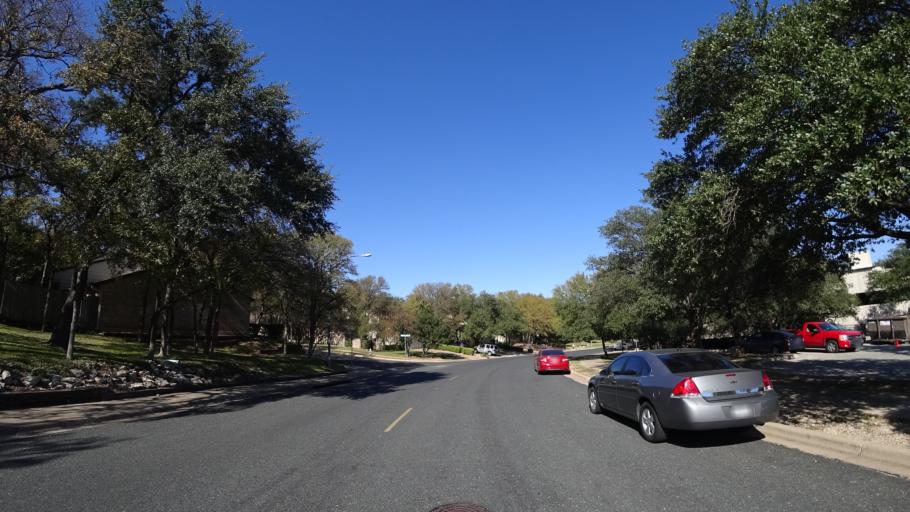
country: US
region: Texas
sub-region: Williamson County
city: Jollyville
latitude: 30.3712
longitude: -97.7439
